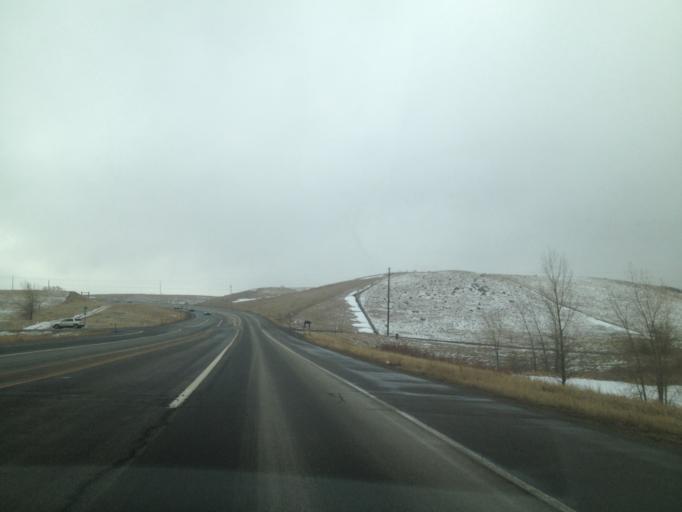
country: US
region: Colorado
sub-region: Jefferson County
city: Golden
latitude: 39.8453
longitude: -105.2347
